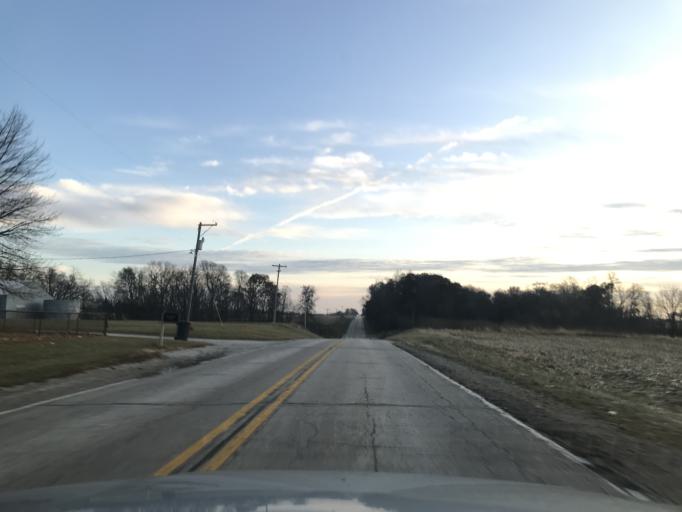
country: US
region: Illinois
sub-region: Henderson County
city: Oquawka
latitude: 40.9550
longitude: -90.8640
